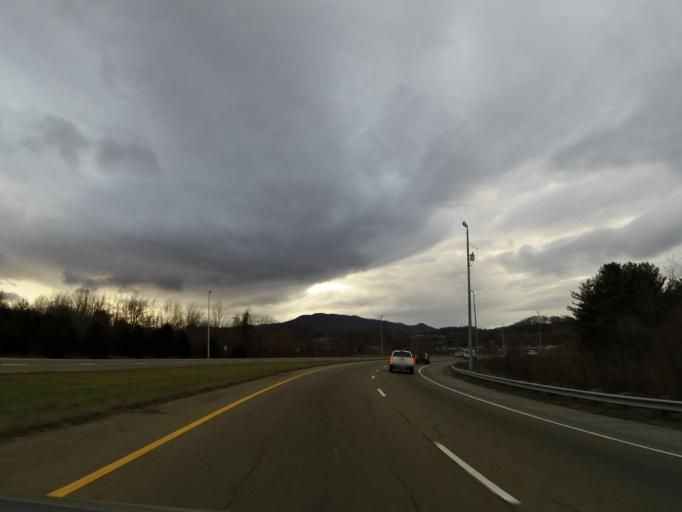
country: US
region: Tennessee
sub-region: Carter County
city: Central
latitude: 36.3190
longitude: -82.2757
